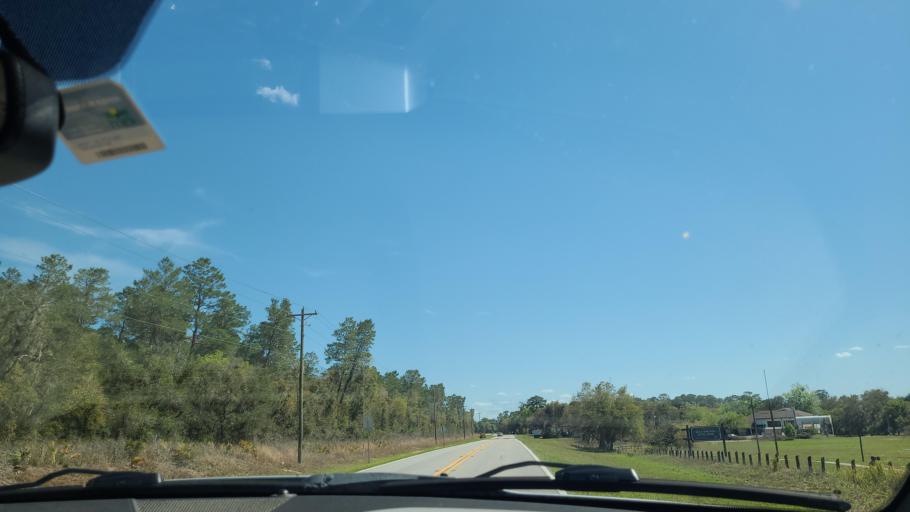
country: US
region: Florida
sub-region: Putnam County
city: Crescent City
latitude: 29.3668
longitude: -81.7410
